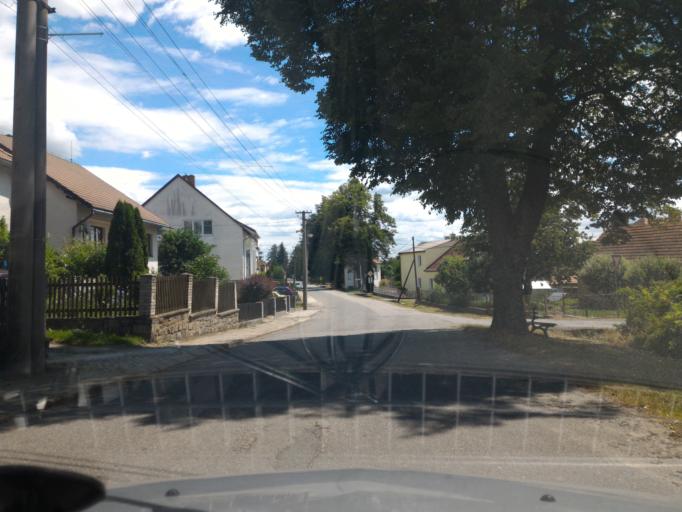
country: CZ
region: Vysocina
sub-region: Okres Jihlava
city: Telc
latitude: 49.2217
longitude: 15.3895
